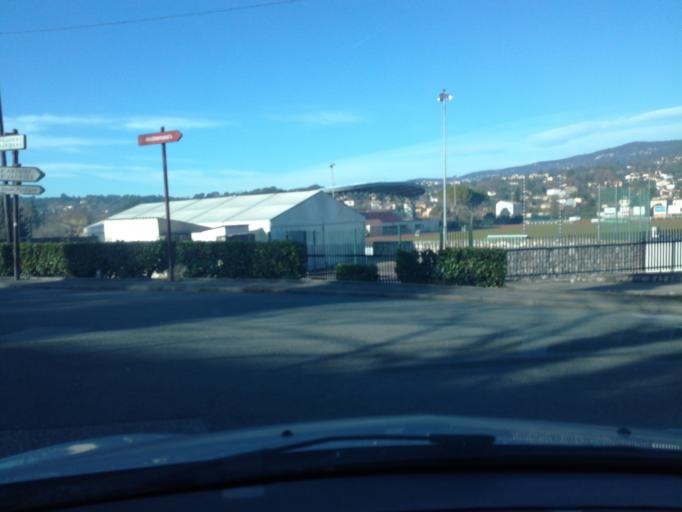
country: FR
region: Provence-Alpes-Cote d'Azur
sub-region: Departement des Alpes-Maritimes
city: Grasse
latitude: 43.6365
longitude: 6.9334
